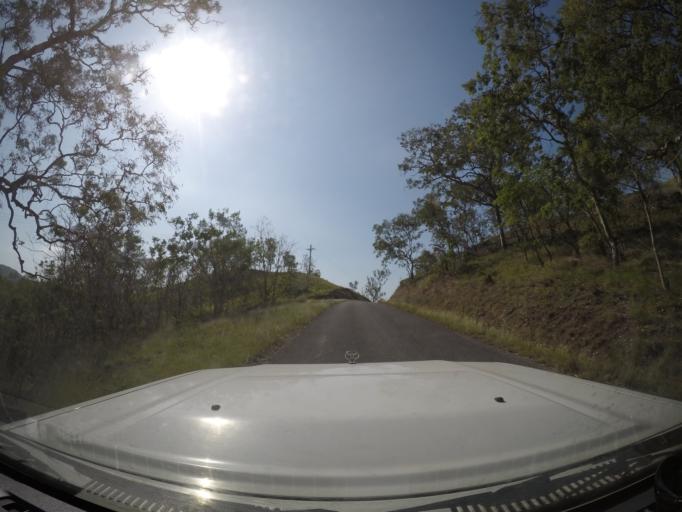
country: PG
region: Central Province
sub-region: Rigo
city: Kwikila
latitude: -9.8685
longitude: 147.5642
